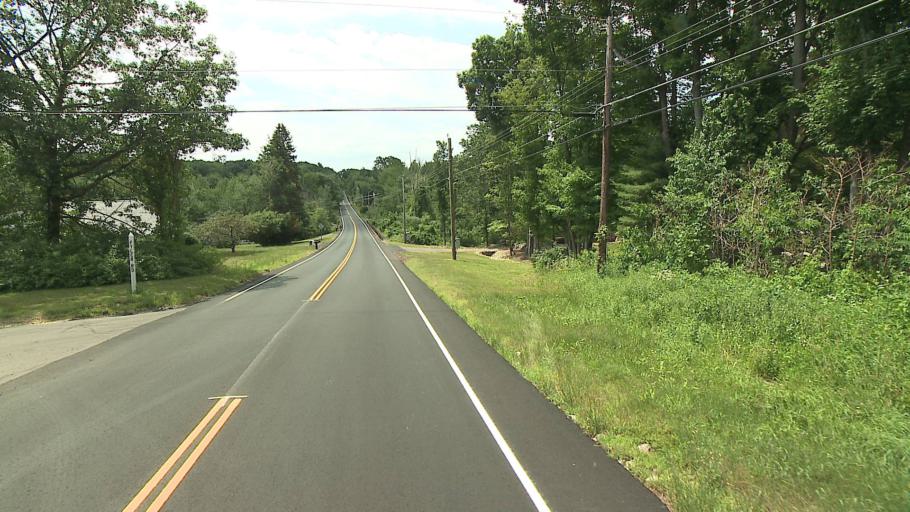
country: US
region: Massachusetts
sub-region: Hampden County
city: Granville
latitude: 42.0291
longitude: -72.8861
